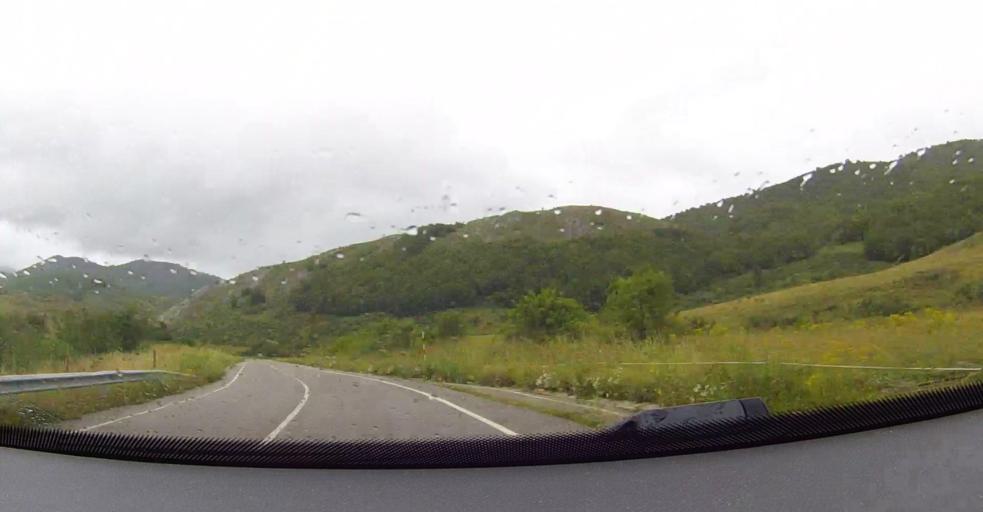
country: ES
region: Castille and Leon
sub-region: Provincia de Leon
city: Marana
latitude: 43.0708
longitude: -5.1483
